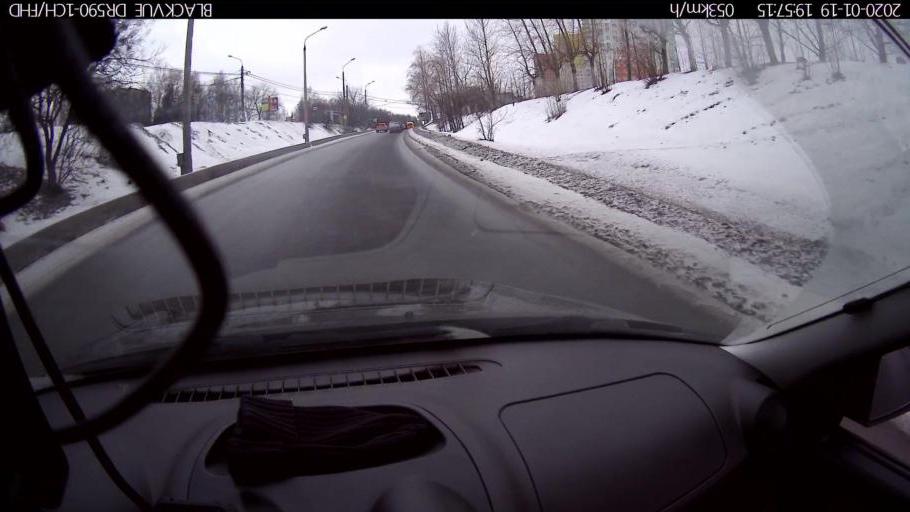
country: RU
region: Nizjnij Novgorod
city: Nizhniy Novgorod
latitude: 56.2410
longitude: 43.9609
